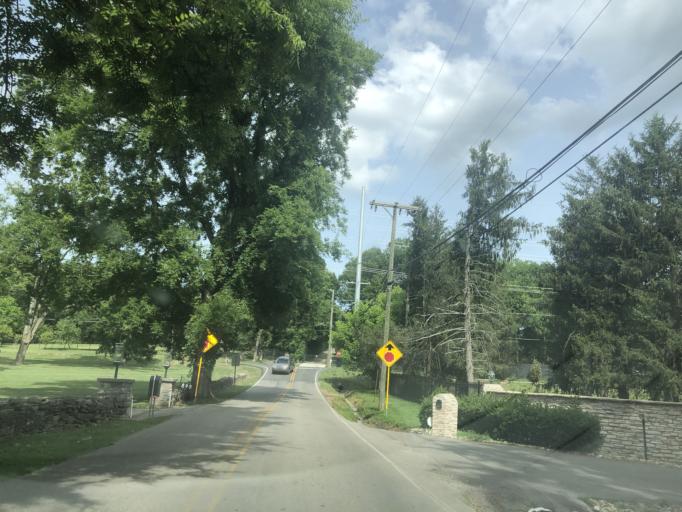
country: US
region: Tennessee
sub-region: Davidson County
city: Oak Hill
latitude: 36.0882
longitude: -86.7727
